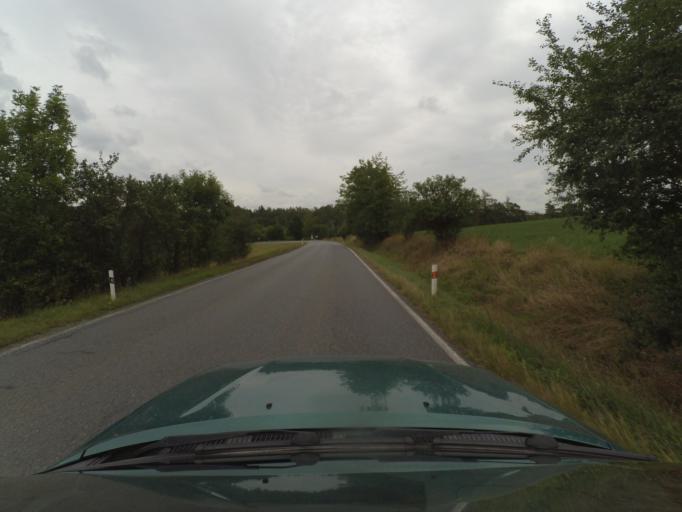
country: CZ
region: Plzensky
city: Kozlany
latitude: 49.9969
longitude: 13.5633
